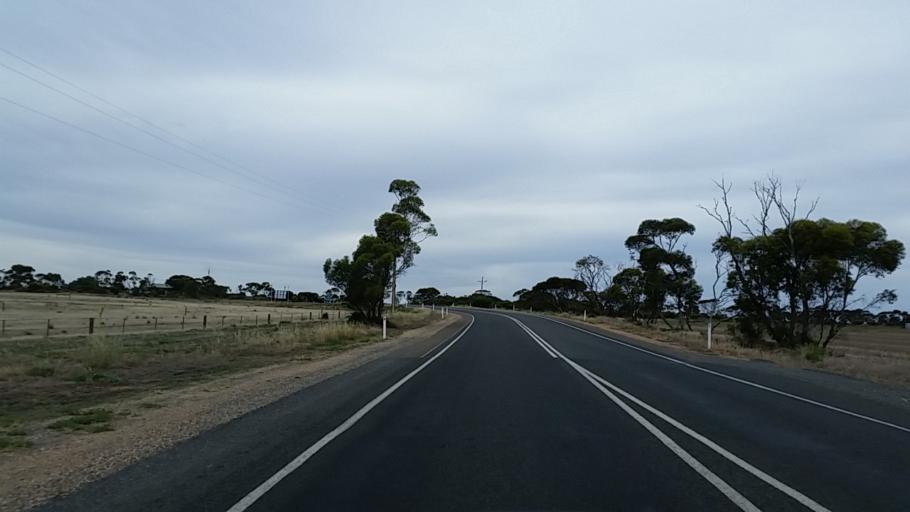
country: AU
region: South Australia
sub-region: Mid Murray
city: Mannum
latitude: -34.9060
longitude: 139.2797
